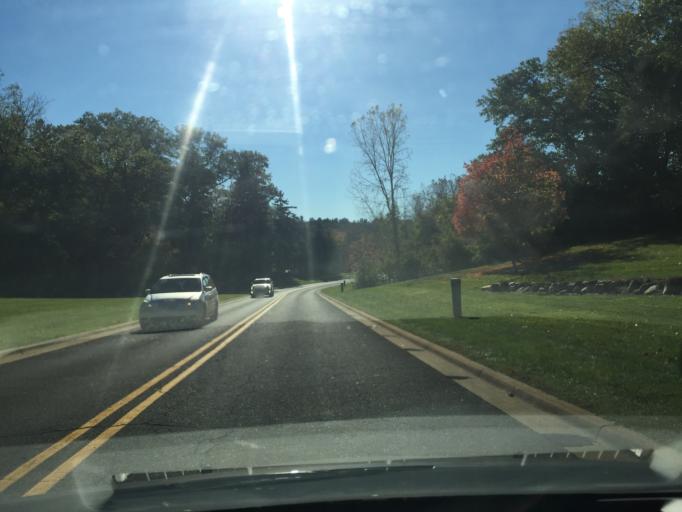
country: US
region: Michigan
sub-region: Oakland County
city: Bloomfield Hills
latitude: 42.5759
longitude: -83.2433
